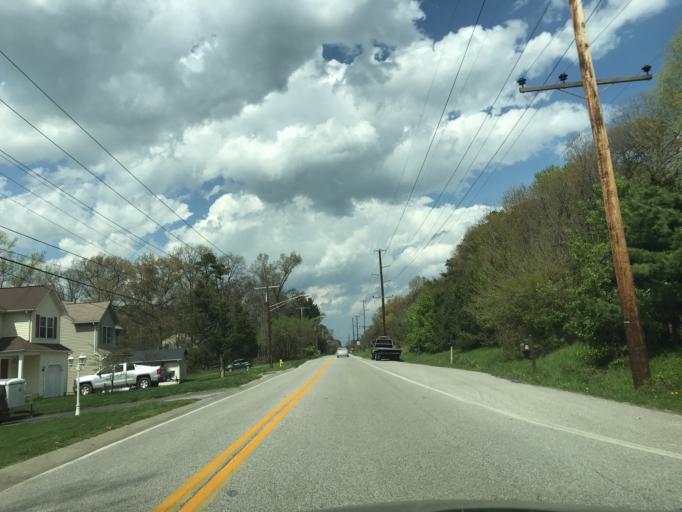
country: US
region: Maryland
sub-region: Anne Arundel County
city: Severn
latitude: 39.1186
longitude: -76.6809
